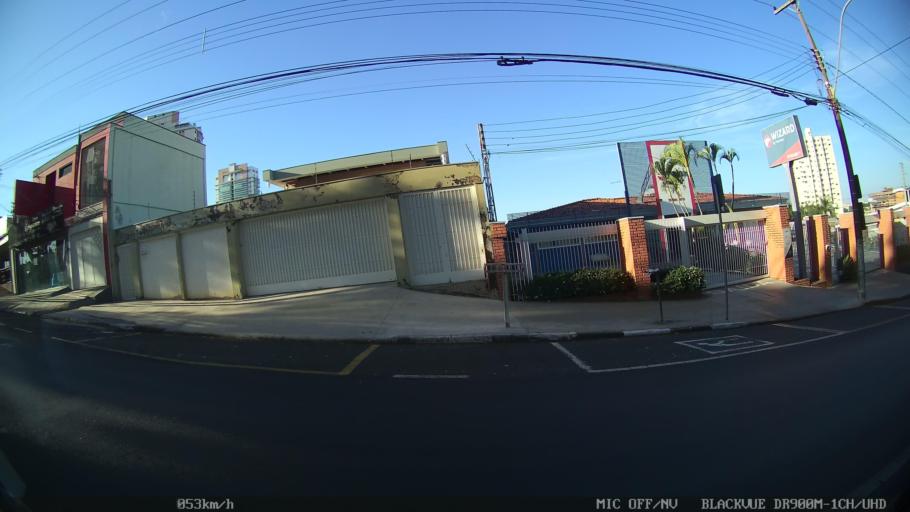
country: BR
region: Sao Paulo
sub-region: Franca
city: Franca
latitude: -20.5360
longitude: -47.3927
